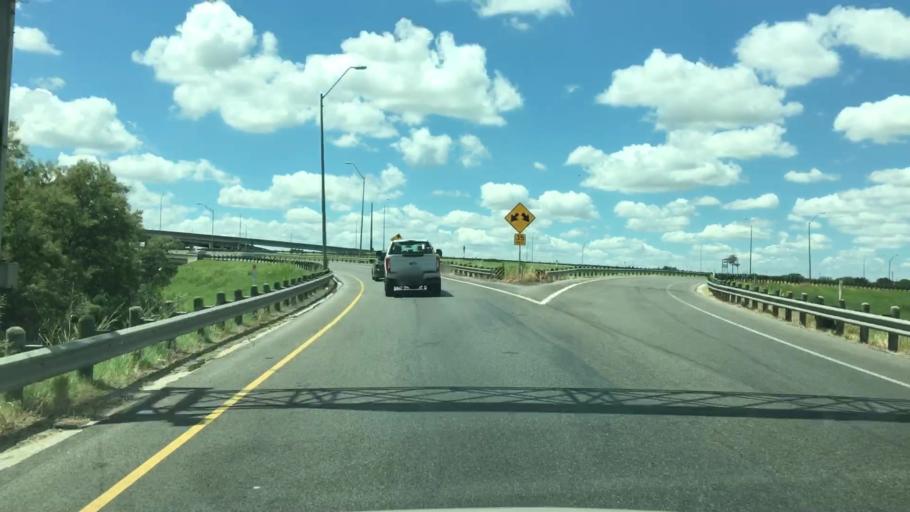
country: US
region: Texas
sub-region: Bexar County
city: China Grove
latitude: 29.3311
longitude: -98.4140
